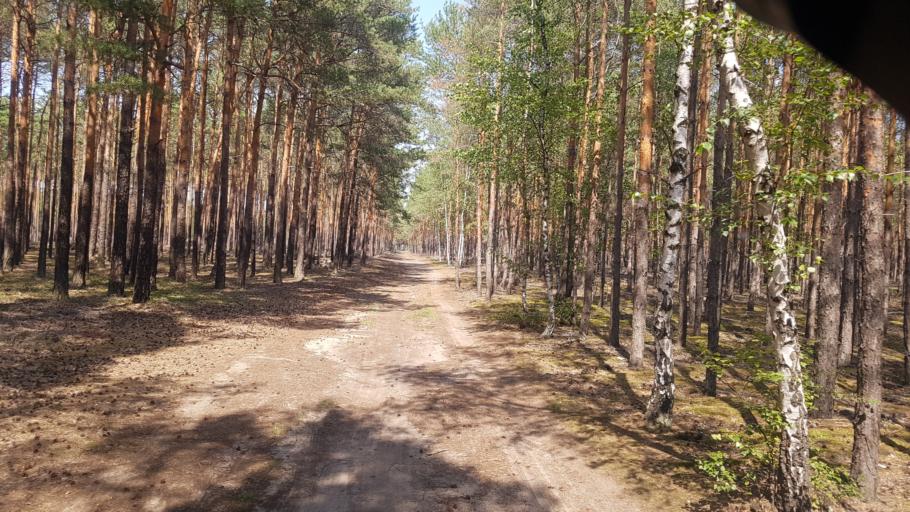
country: DE
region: Brandenburg
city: Spremberg
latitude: 51.6393
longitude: 14.4098
